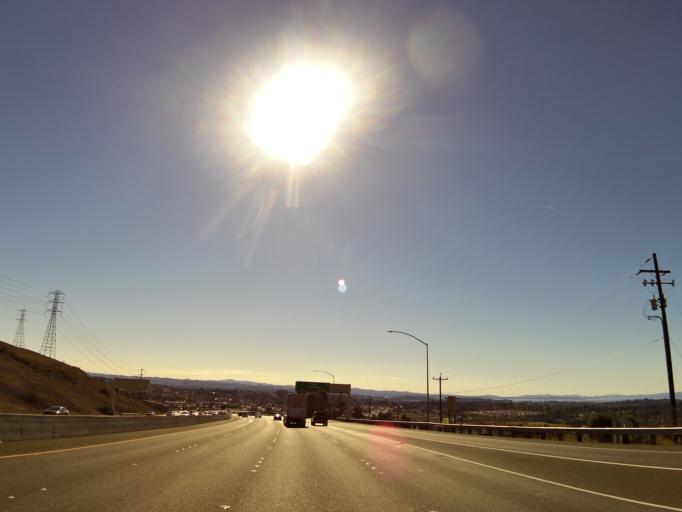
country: US
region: California
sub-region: Napa County
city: American Canyon
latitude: 38.1512
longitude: -122.2168
